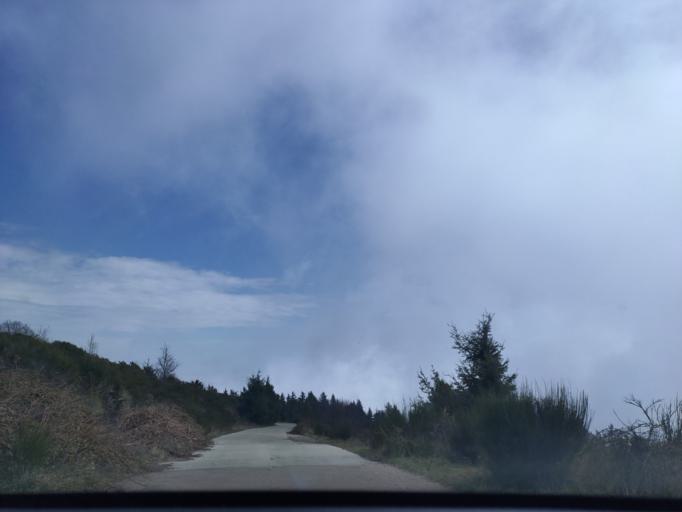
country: ES
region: Catalonia
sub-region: Provincia de Barcelona
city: Fogars de Montclus
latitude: 41.7614
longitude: 2.4566
